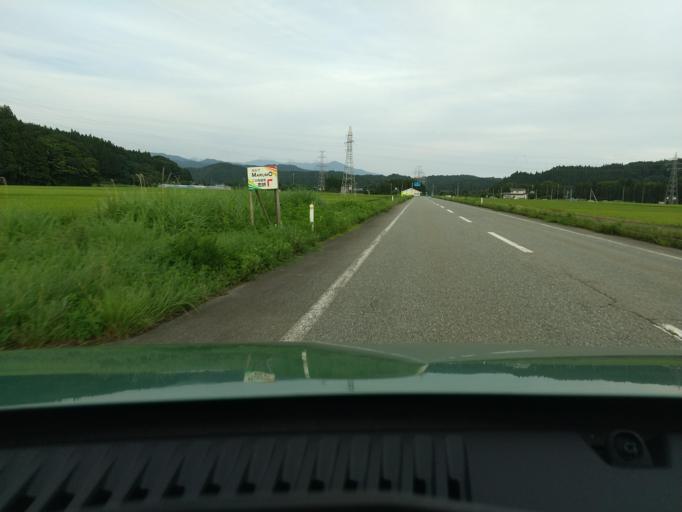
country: JP
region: Akita
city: Akita Shi
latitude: 39.7927
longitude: 140.1077
